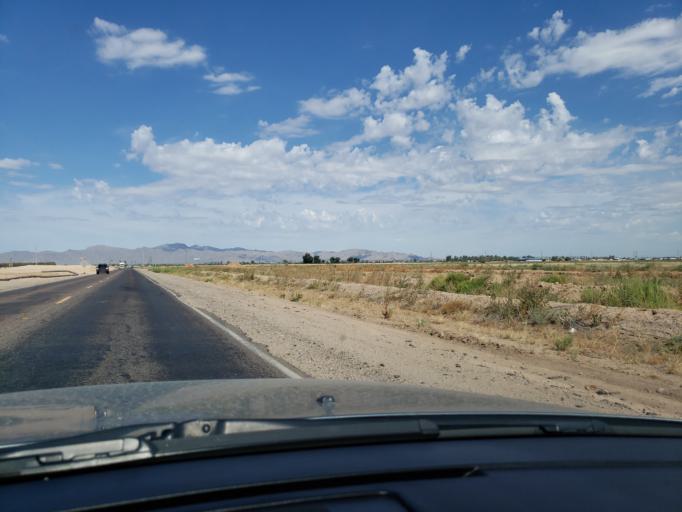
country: US
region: Arizona
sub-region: Maricopa County
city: Youngtown
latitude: 33.5511
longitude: -112.3347
